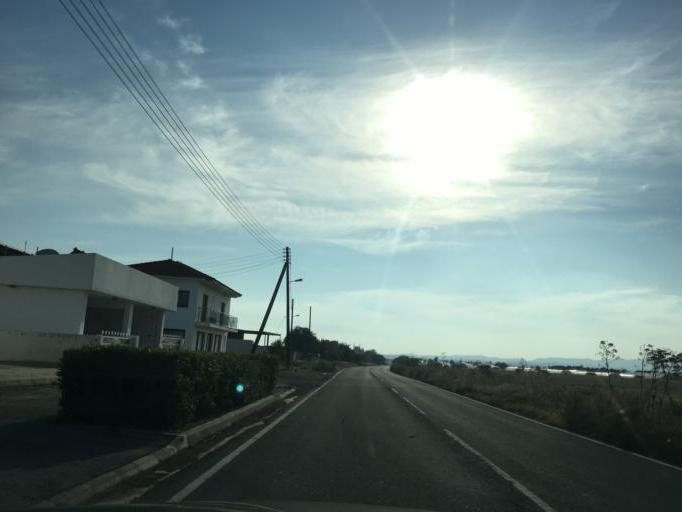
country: CY
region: Larnaka
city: Kofinou
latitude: 34.7332
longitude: 33.3607
